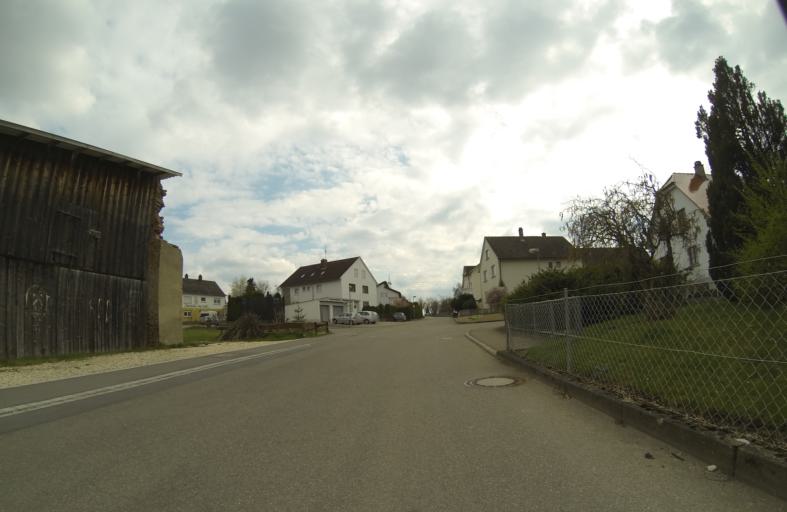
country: DE
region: Baden-Wuerttemberg
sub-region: Tuebingen Region
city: Erbach
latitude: 48.2994
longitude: 9.9003
